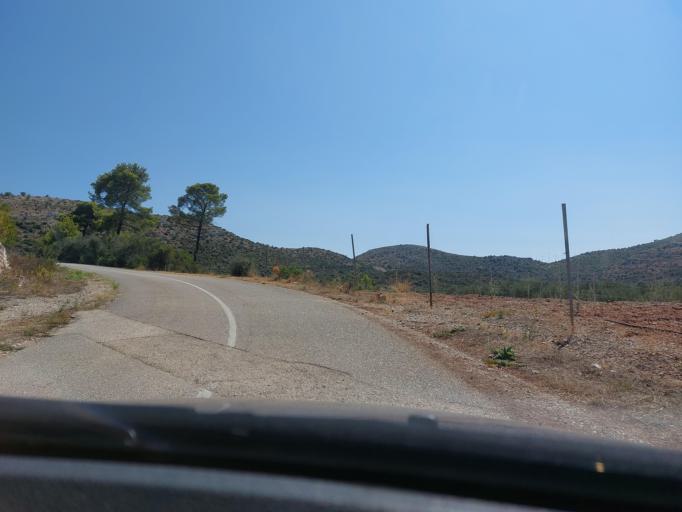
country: HR
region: Dubrovacko-Neretvanska
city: Smokvica
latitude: 42.7523
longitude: 16.8778
